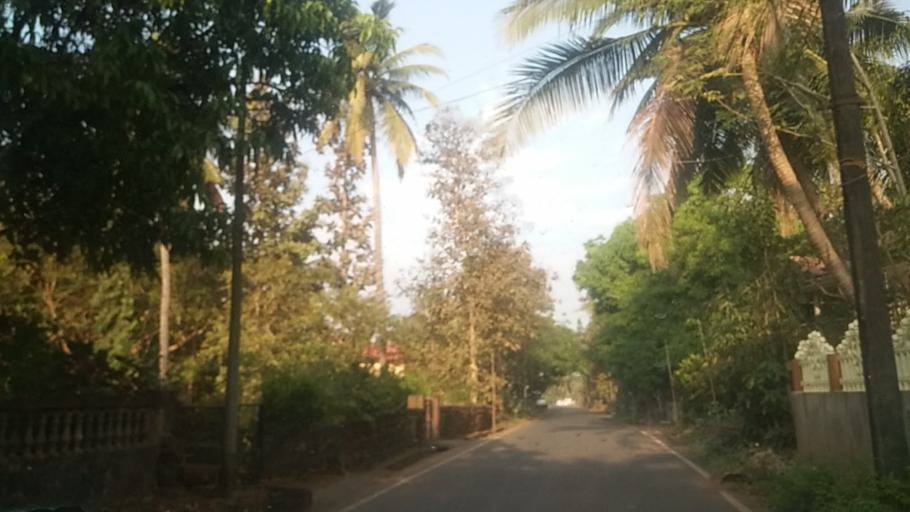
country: IN
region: Goa
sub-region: South Goa
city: Chinchinim
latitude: 15.2366
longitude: 73.9824
